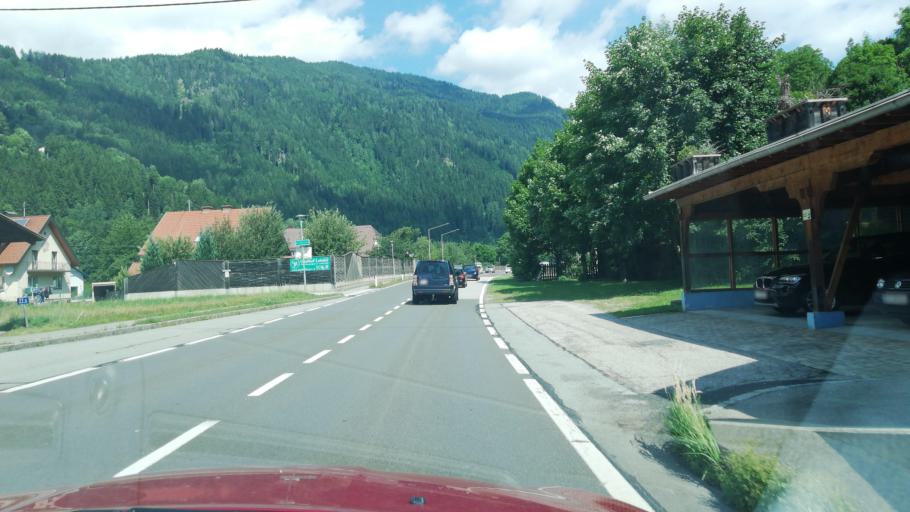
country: AT
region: Styria
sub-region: Politischer Bezirk Murau
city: Durnstein in der Steiermark
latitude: 46.9894
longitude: 14.3899
